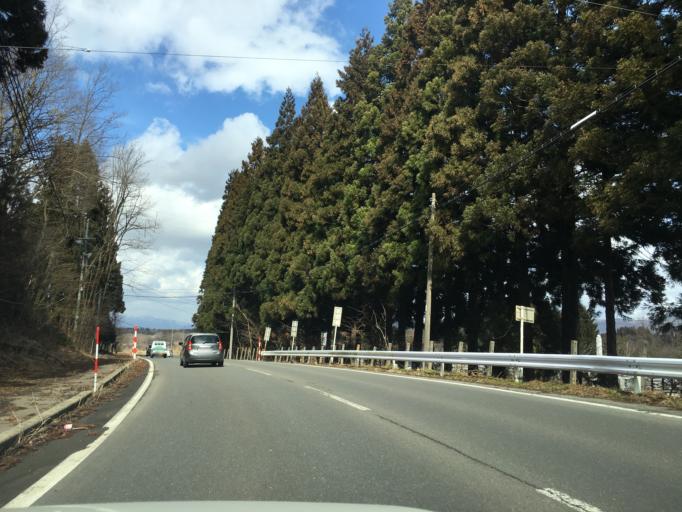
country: JP
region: Akita
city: Odate
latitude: 40.2025
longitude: 140.5554
